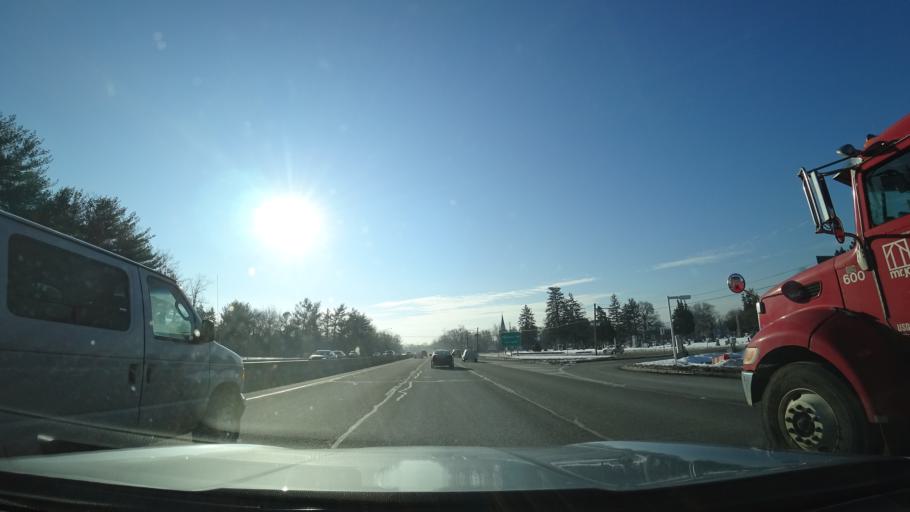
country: US
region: New Jersey
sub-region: Bergen County
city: Ho-Ho-Kus
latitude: 40.9878
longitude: -74.0936
